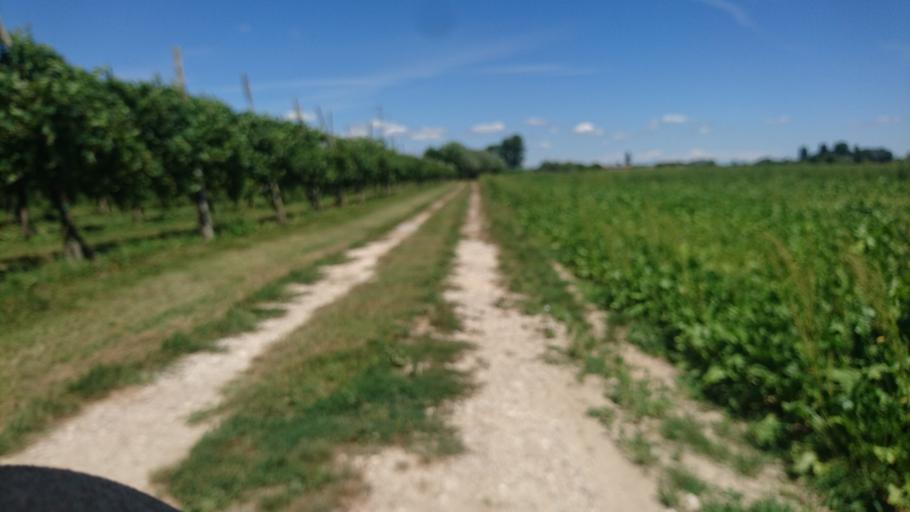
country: IT
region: Veneto
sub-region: Provincia di Padova
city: Polverara
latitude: 45.3134
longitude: 11.9747
